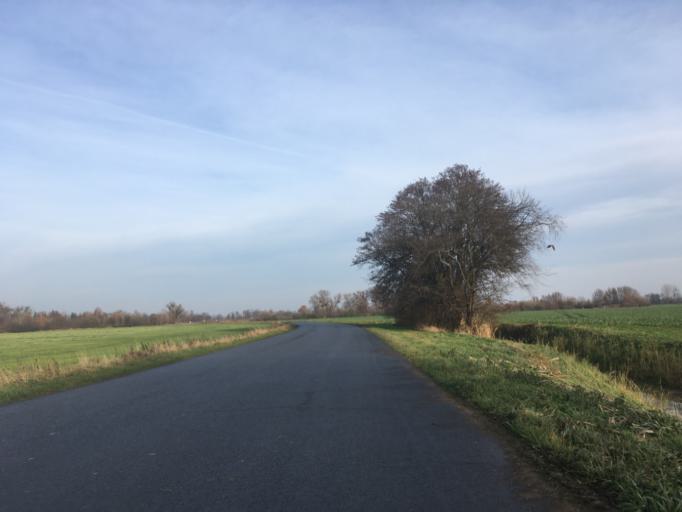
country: DE
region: Brandenburg
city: Bad Freienwalde
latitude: 52.7794
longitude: 14.0811
